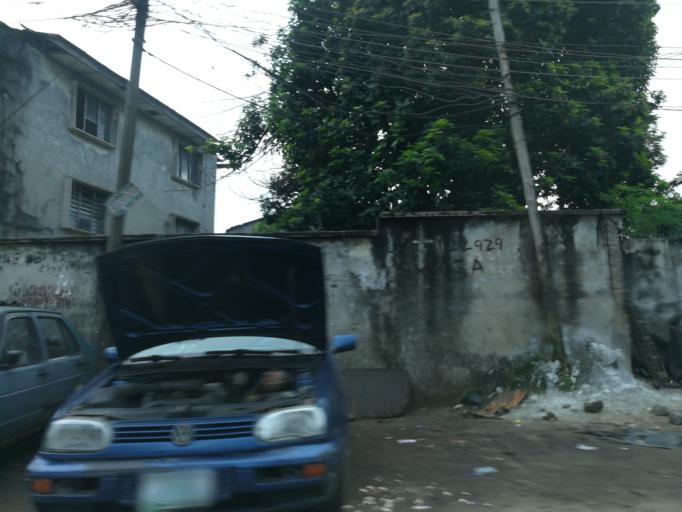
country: NG
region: Rivers
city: Port Harcourt
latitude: 4.7638
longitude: 7.0139
